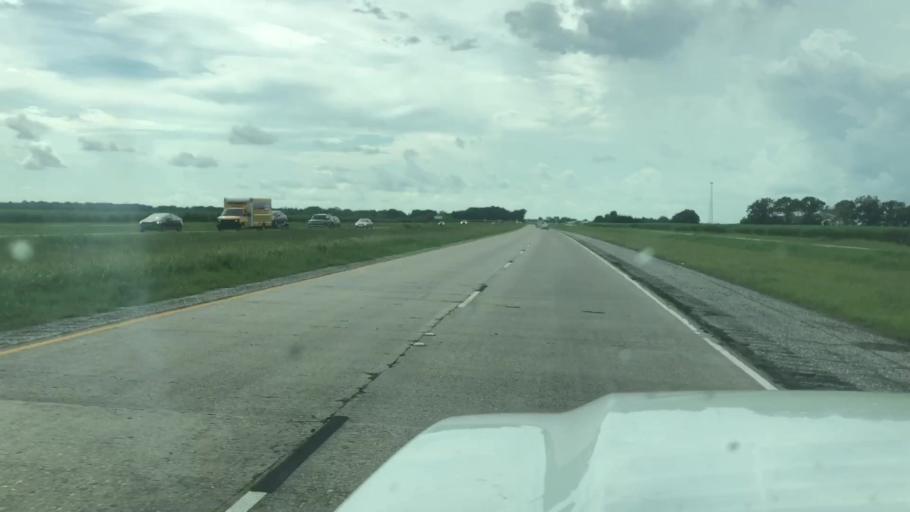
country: US
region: Louisiana
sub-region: Iberia Parish
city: Jeanerette
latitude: 29.8582
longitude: -91.6140
